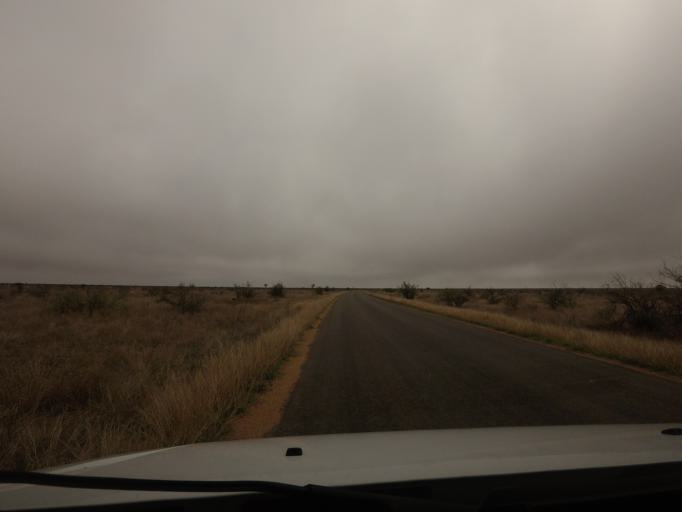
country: ZA
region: Limpopo
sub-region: Mopani District Municipality
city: Phalaborwa
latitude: -24.2387
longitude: 31.7198
